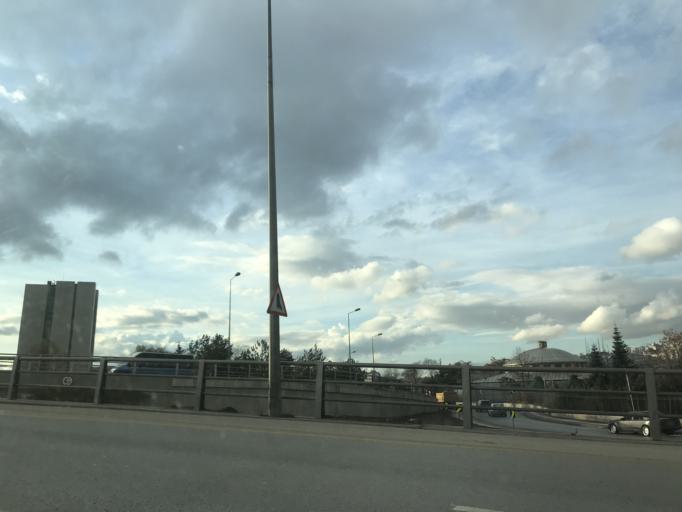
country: TR
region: Ankara
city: Ankara
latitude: 39.9524
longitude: 32.8365
